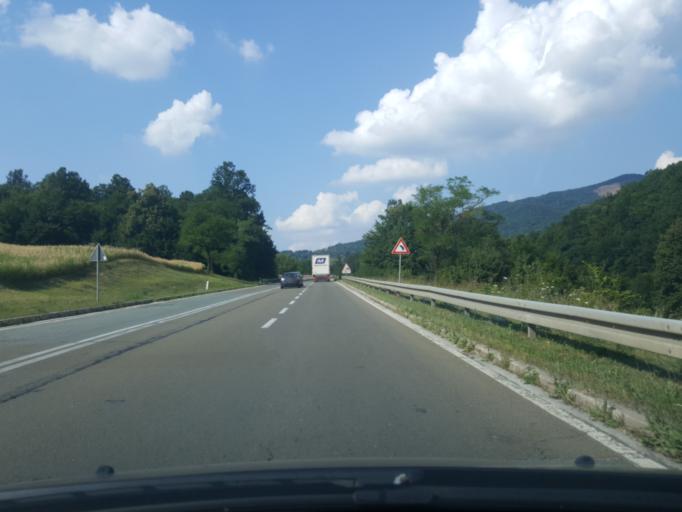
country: RS
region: Central Serbia
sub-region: Moravicki Okrug
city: Gornji Milanovac
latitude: 44.1119
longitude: 20.4838
